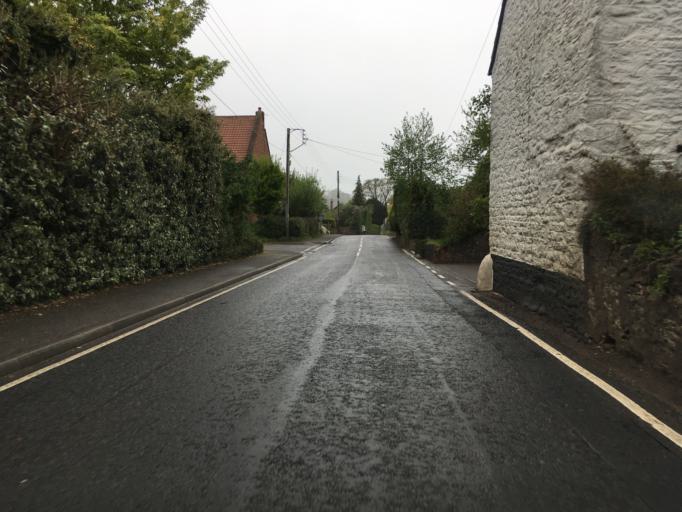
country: GB
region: England
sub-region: Bath and North East Somerset
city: Compton Martin
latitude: 51.3114
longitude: -2.6588
